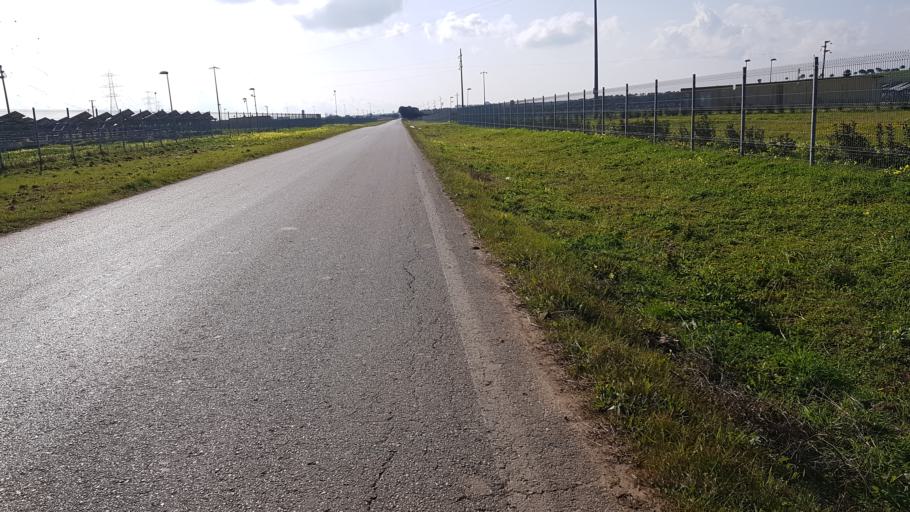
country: IT
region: Apulia
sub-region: Provincia di Brindisi
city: La Rosa
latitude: 40.5895
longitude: 17.9030
